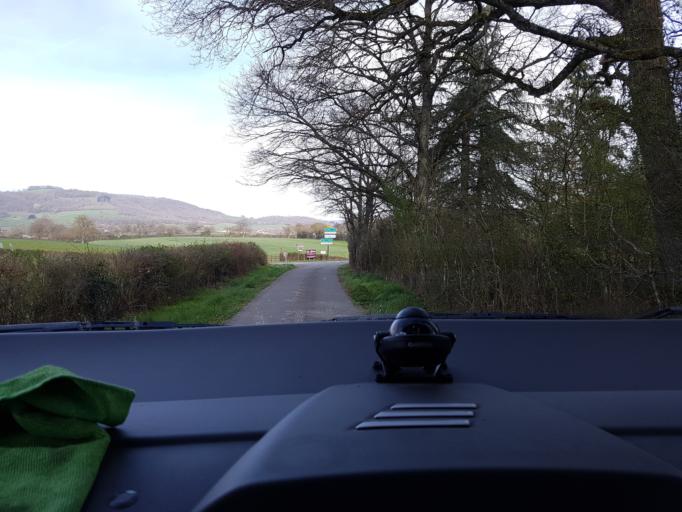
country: FR
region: Bourgogne
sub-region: Departement de Saone-et-Loire
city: Toulon-sur-Arroux
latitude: 46.7571
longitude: 4.1370
